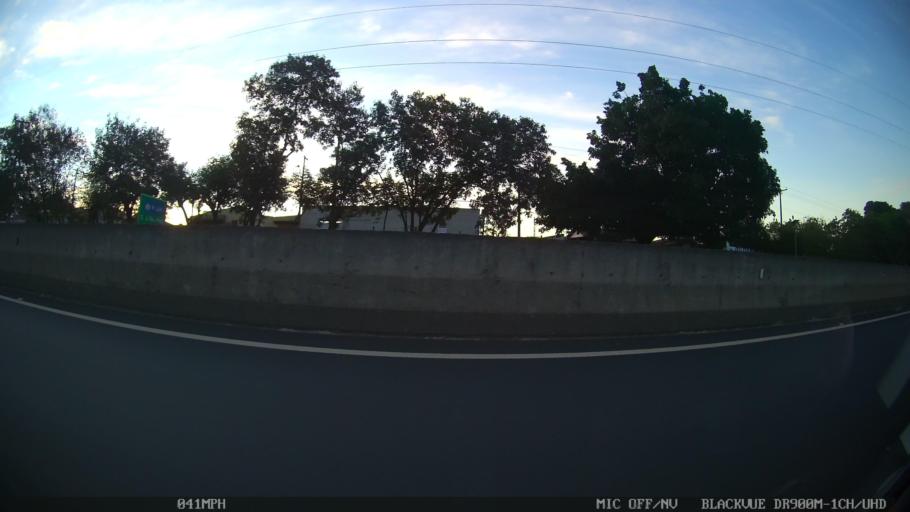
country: BR
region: Sao Paulo
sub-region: Catanduva
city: Catanduva
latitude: -21.1307
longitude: -49.0135
